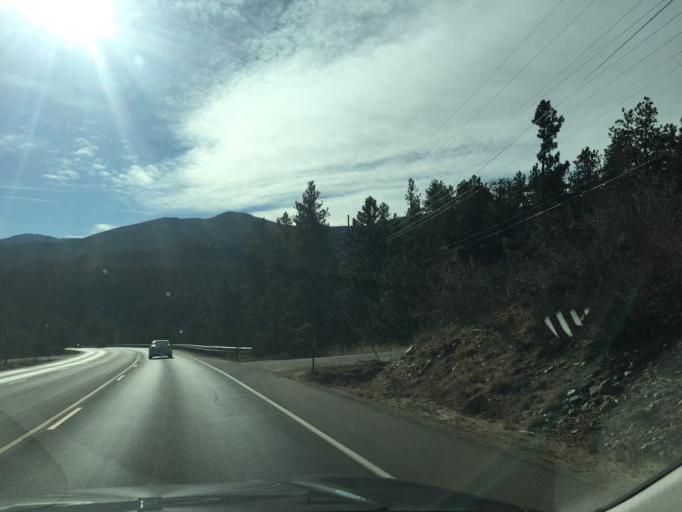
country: US
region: Colorado
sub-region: Jefferson County
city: Evergreen
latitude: 39.4115
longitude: -105.4741
